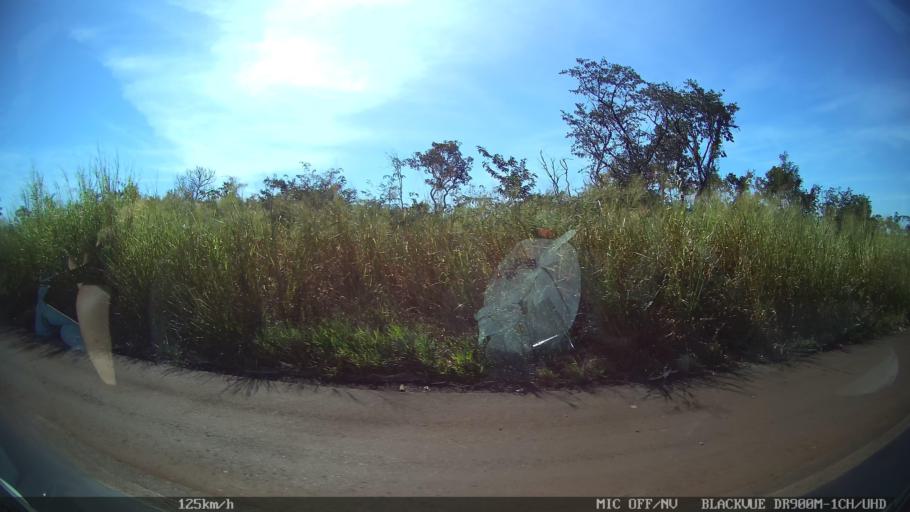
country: BR
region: Sao Paulo
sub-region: Ipua
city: Ipua
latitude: -20.5009
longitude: -47.9506
